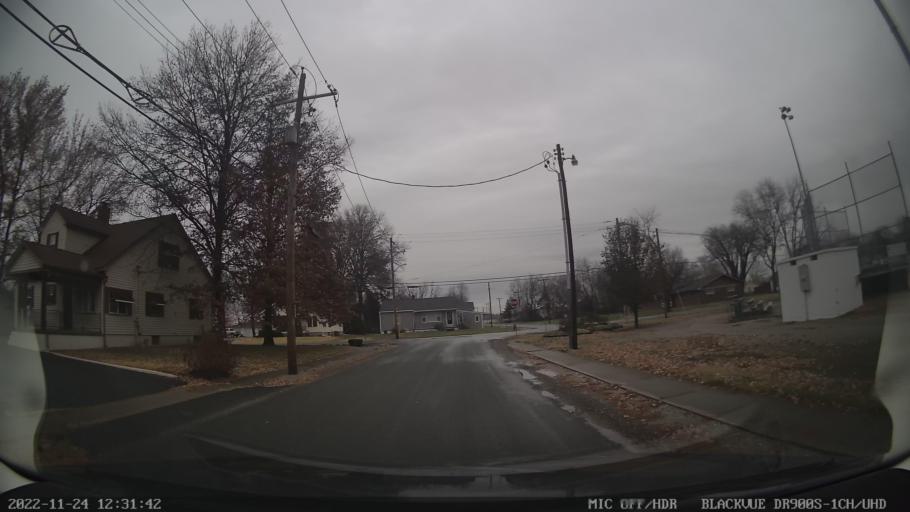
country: US
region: Illinois
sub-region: Macoupin County
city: Staunton
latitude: 39.0183
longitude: -89.7818
